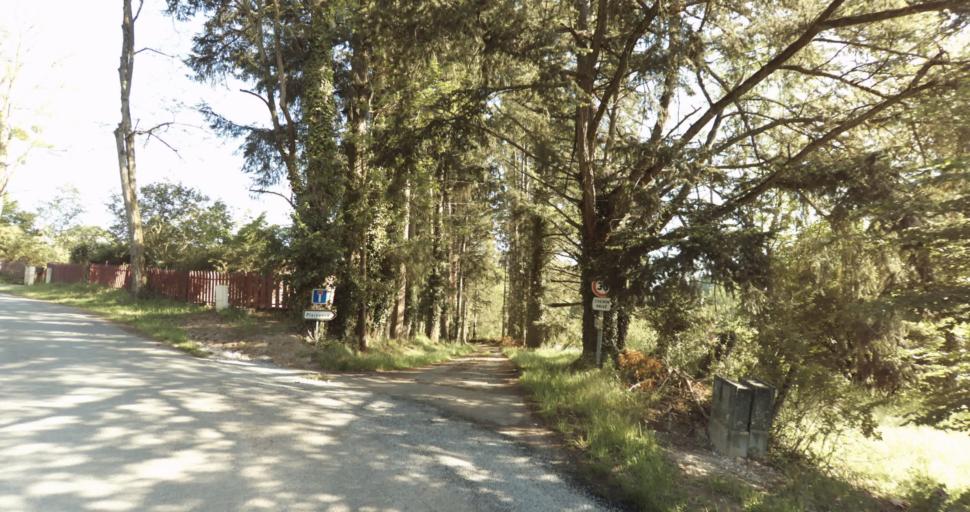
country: FR
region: Limousin
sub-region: Departement de la Haute-Vienne
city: Solignac
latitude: 45.7381
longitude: 1.2759
